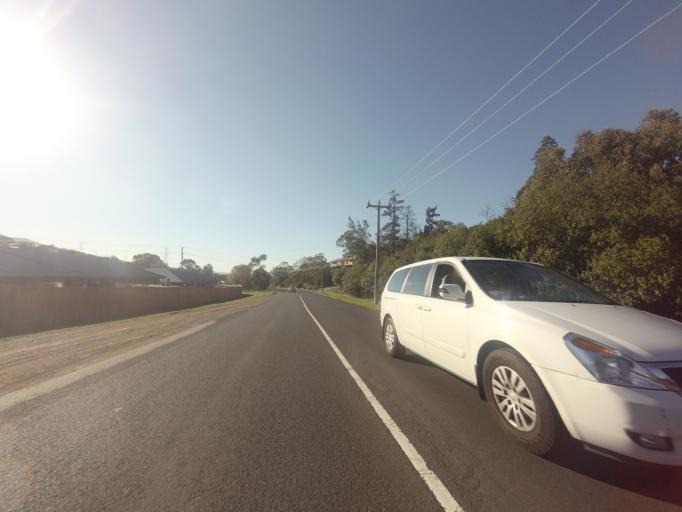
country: AU
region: Tasmania
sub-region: Glenorchy
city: West Moonah
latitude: -42.8536
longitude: 147.2682
